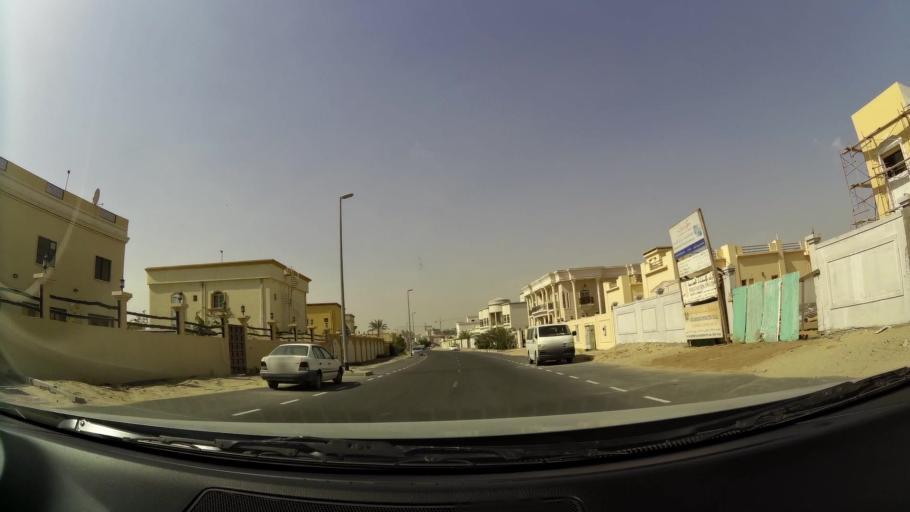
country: AE
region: Ash Shariqah
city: Sharjah
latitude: 25.2026
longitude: 55.4049
